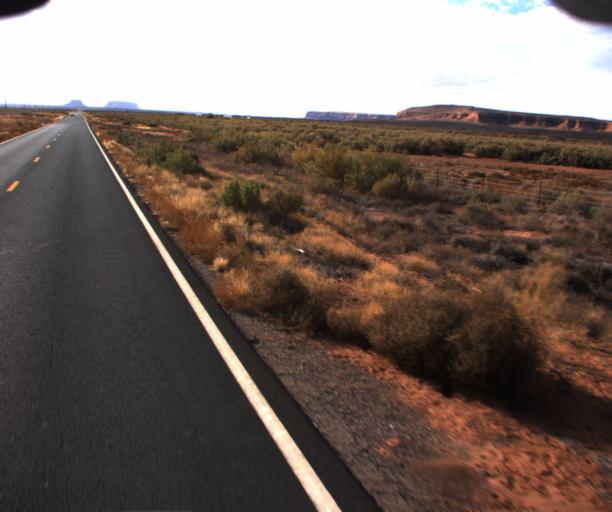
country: US
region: Arizona
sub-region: Apache County
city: Many Farms
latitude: 36.6754
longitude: -109.6009
